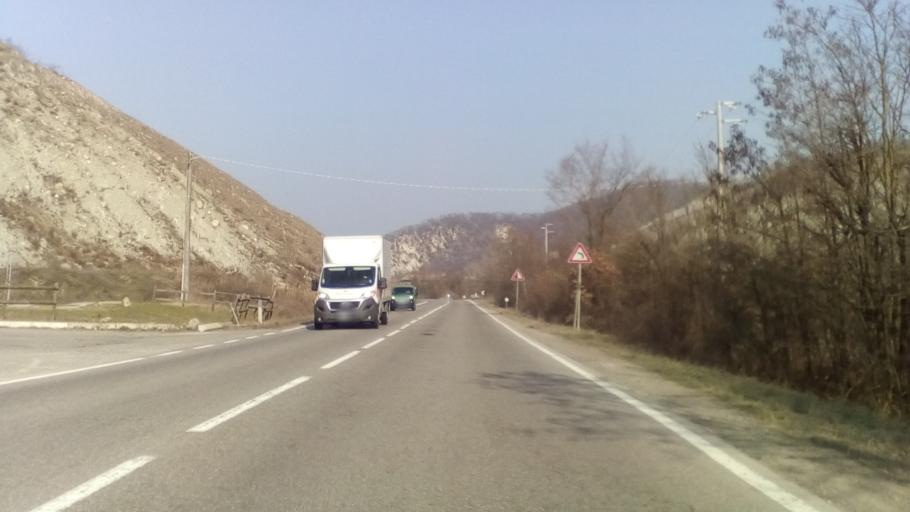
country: IT
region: Emilia-Romagna
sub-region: Provincia di Modena
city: Gorzano
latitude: 44.4717
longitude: 10.8455
